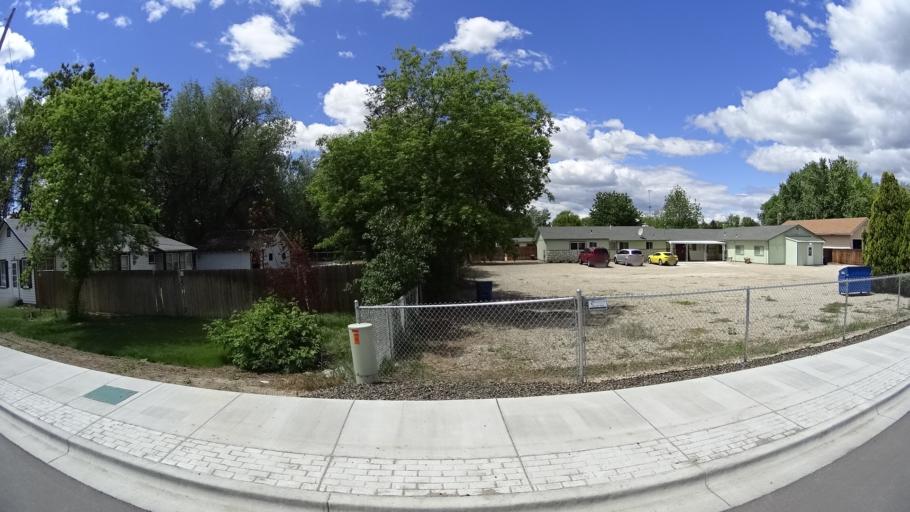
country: US
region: Idaho
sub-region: Ada County
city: Eagle
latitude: 43.6436
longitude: -116.3344
